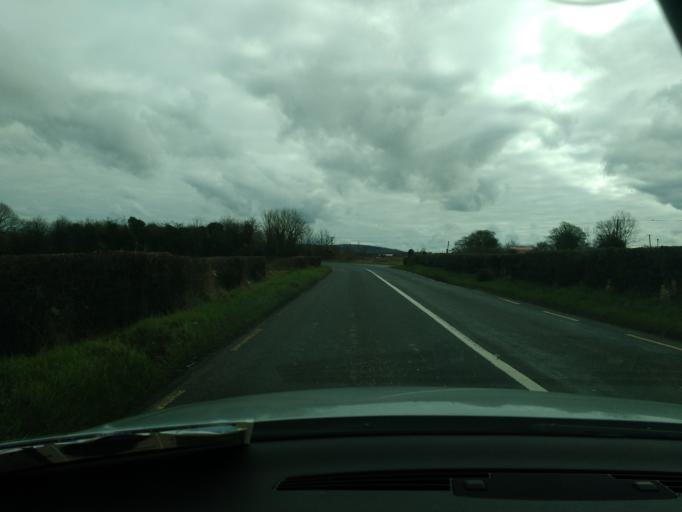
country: IE
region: Leinster
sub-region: Laois
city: Rathdowney
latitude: 52.7198
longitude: -7.5358
